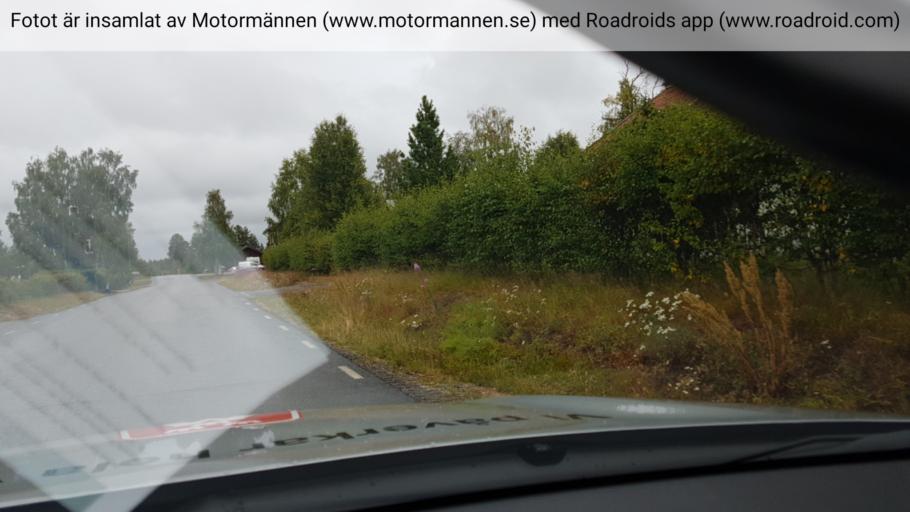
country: SE
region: Norrbotten
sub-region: Gallivare Kommun
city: Gaellivare
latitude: 66.7536
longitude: 20.9488
